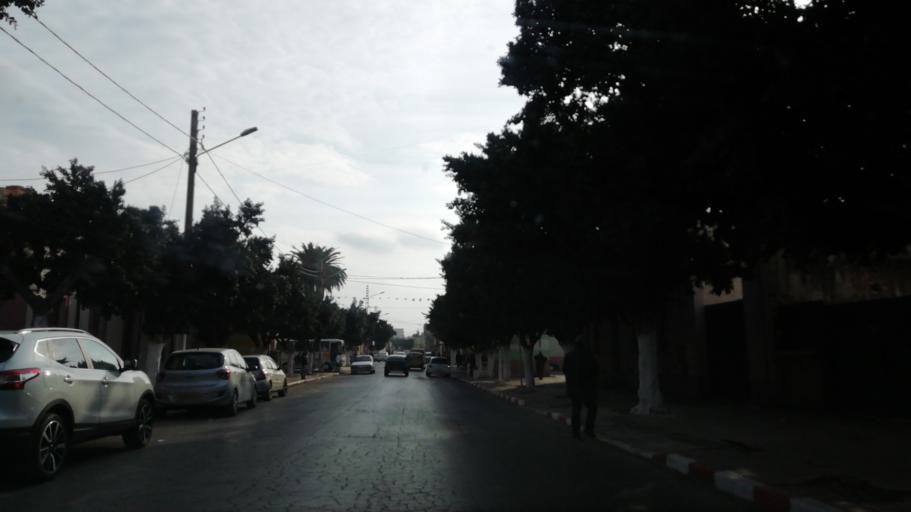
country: DZ
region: Mostaganem
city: Mostaganem
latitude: 35.8597
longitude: 0.0730
